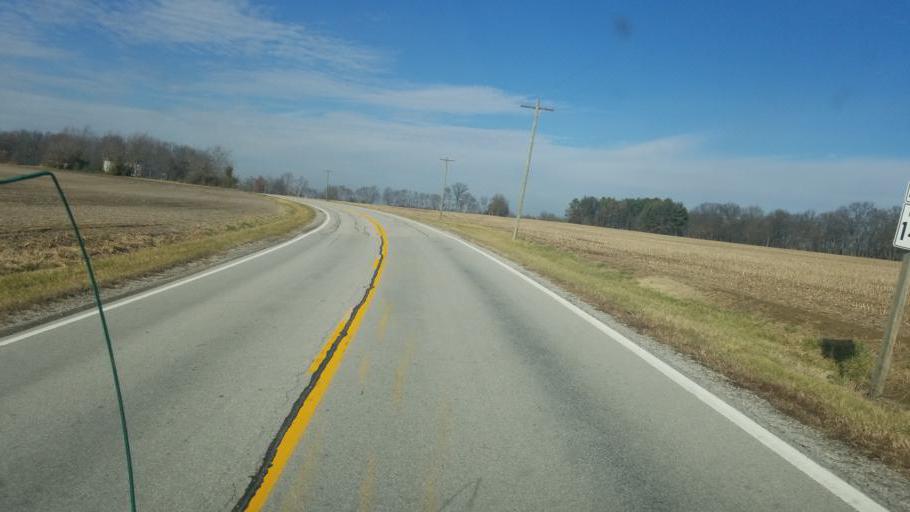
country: US
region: Illinois
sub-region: Saline County
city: Eldorado
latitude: 37.9073
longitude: -88.4531
